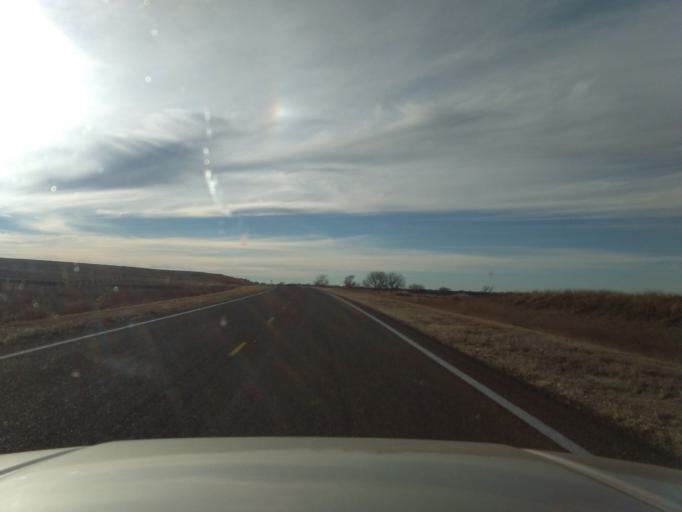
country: US
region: Kansas
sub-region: Norton County
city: Norton
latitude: 39.7510
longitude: -100.1432
